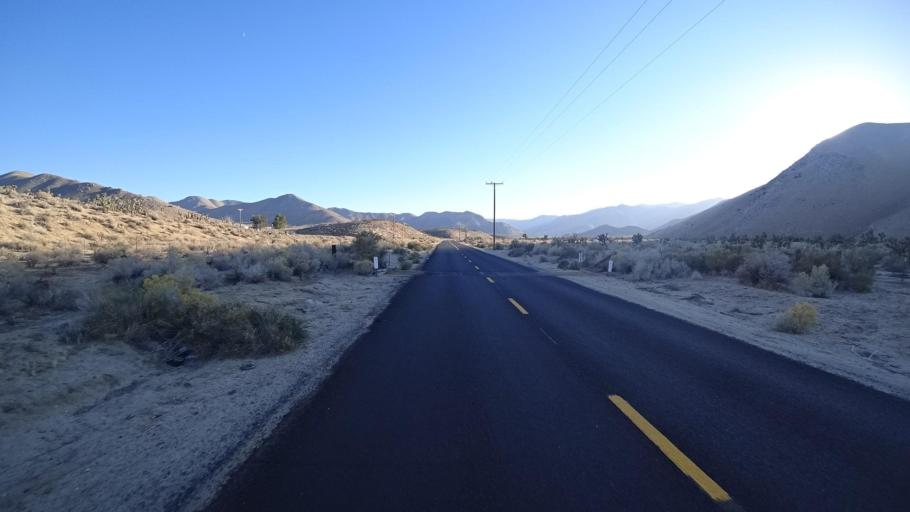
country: US
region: California
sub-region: Kern County
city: Weldon
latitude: 35.6147
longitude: -118.2433
